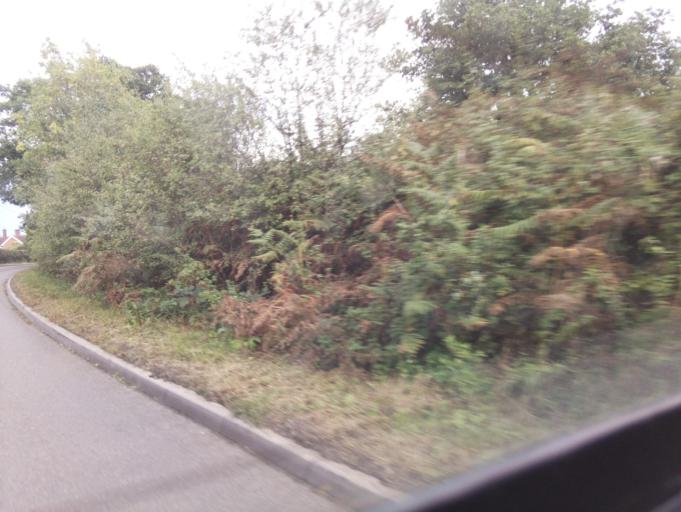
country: GB
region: England
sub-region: Staffordshire
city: Eccleshall
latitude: 52.8390
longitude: -2.2665
